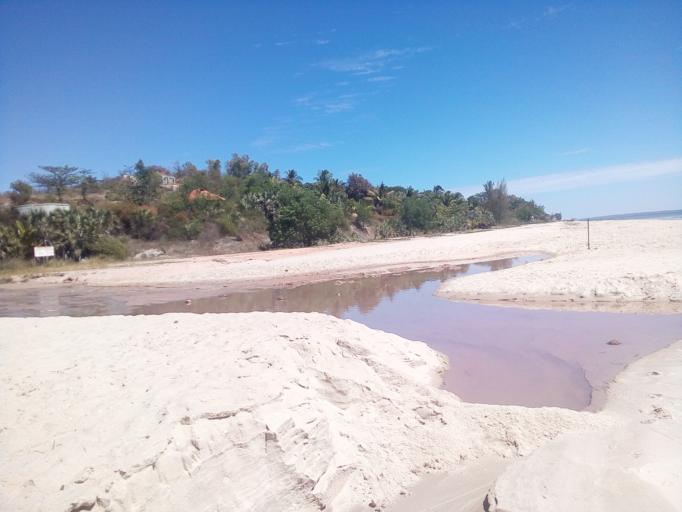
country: MG
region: Boeny
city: Mahajanga
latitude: -15.6298
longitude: 46.3497
